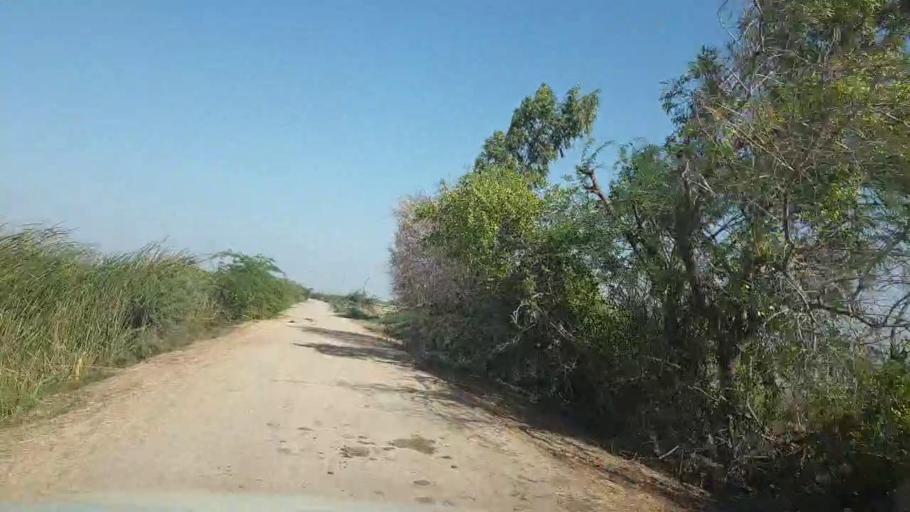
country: PK
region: Sindh
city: Chuhar Jamali
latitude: 24.4649
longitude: 67.8623
